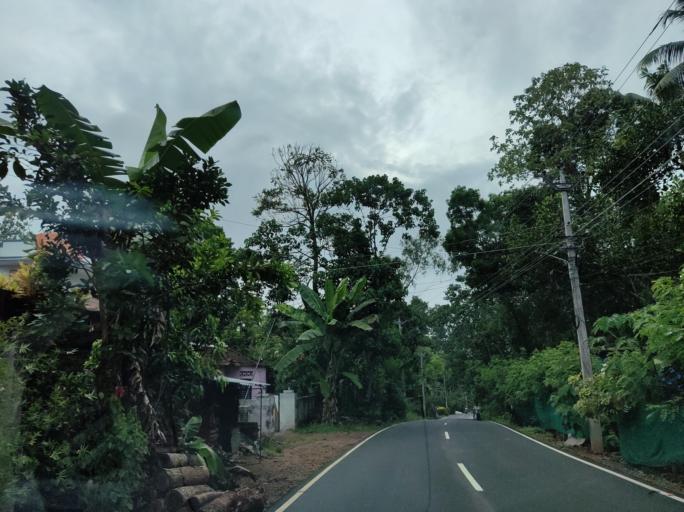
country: IN
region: Kerala
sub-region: Alappuzha
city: Mavelikara
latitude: 9.2306
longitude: 76.5650
